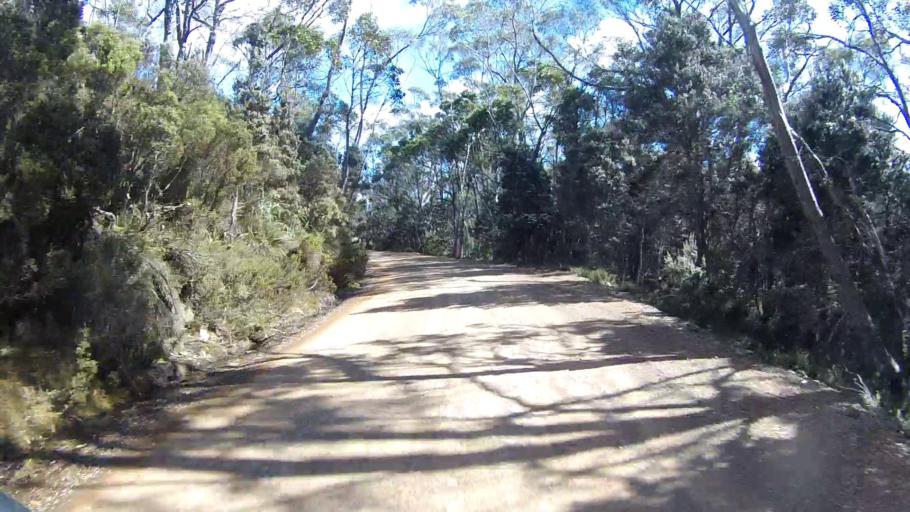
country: AU
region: Tasmania
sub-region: Derwent Valley
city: New Norfolk
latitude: -42.6864
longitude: 146.5941
